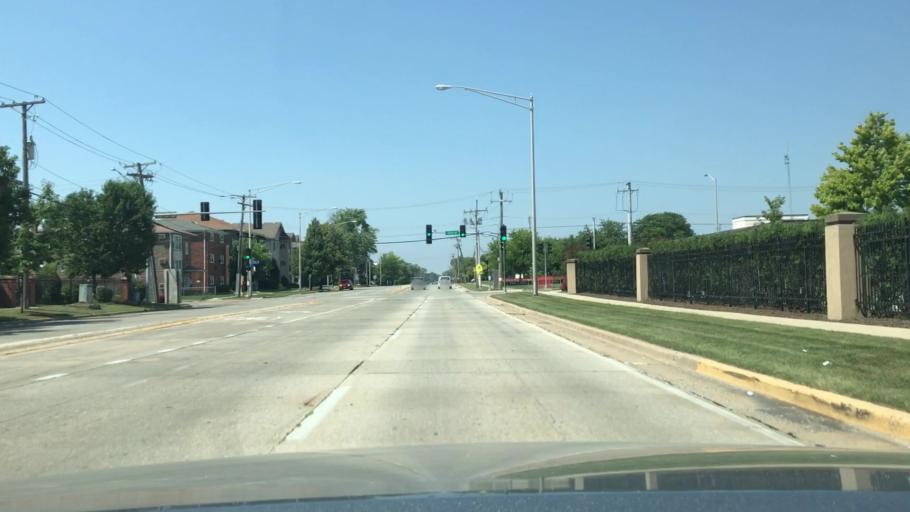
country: US
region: Illinois
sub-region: Cook County
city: Oak Lawn
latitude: 41.6973
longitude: -87.7594
